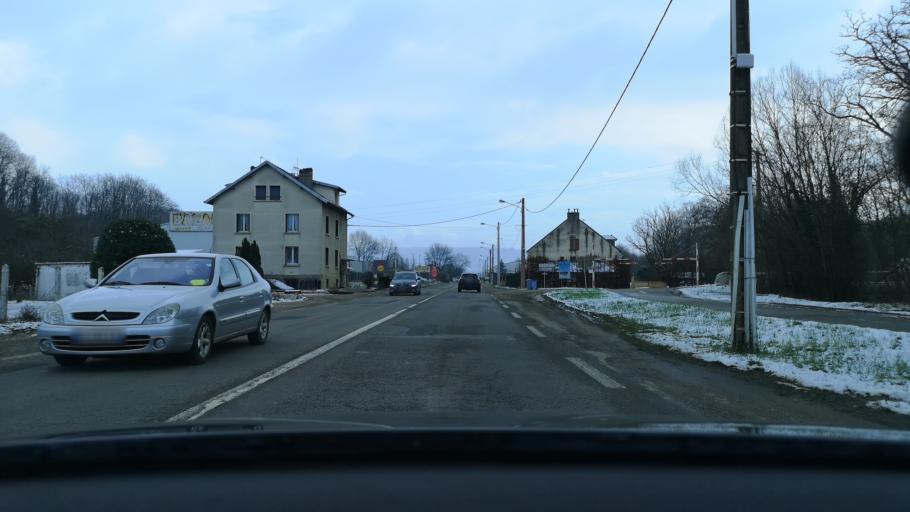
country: FR
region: Franche-Comte
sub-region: Departement du Jura
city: Montmorot
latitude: 46.6776
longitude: 5.5144
